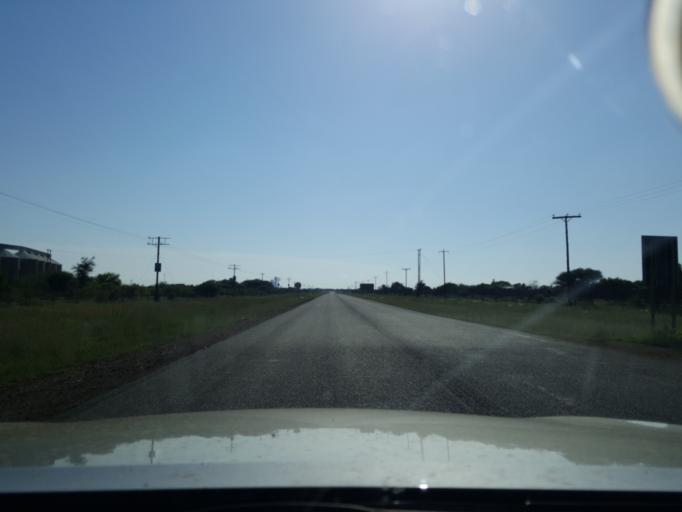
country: ZA
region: North-West
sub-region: Ngaka Modiri Molema District Municipality
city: Mahikeng
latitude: -25.8300
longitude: 25.7915
